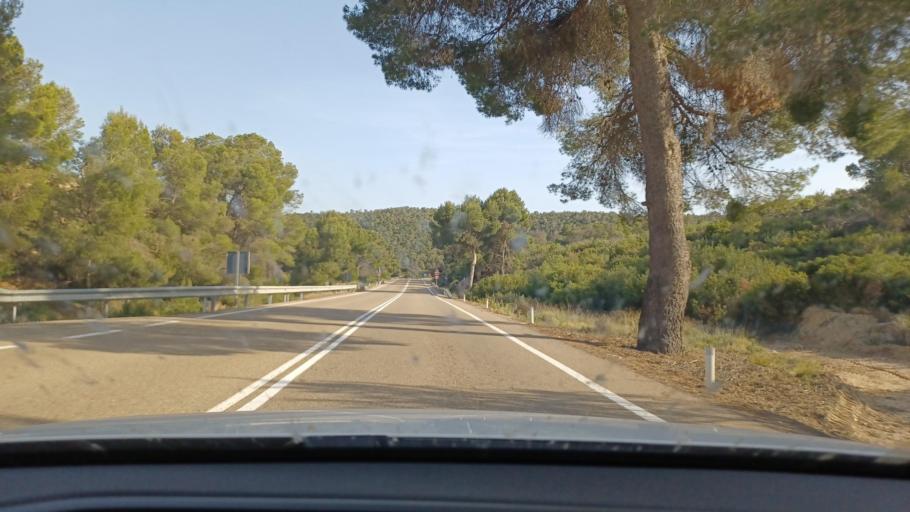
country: ES
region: Aragon
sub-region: Provincia de Zaragoza
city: Chiprana
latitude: 41.3570
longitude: -0.1005
